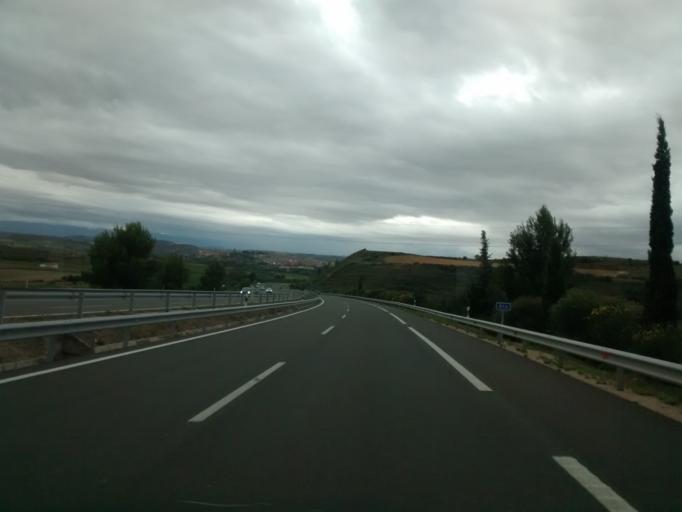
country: ES
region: La Rioja
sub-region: Provincia de La Rioja
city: Brinas
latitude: 42.6065
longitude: -2.8585
